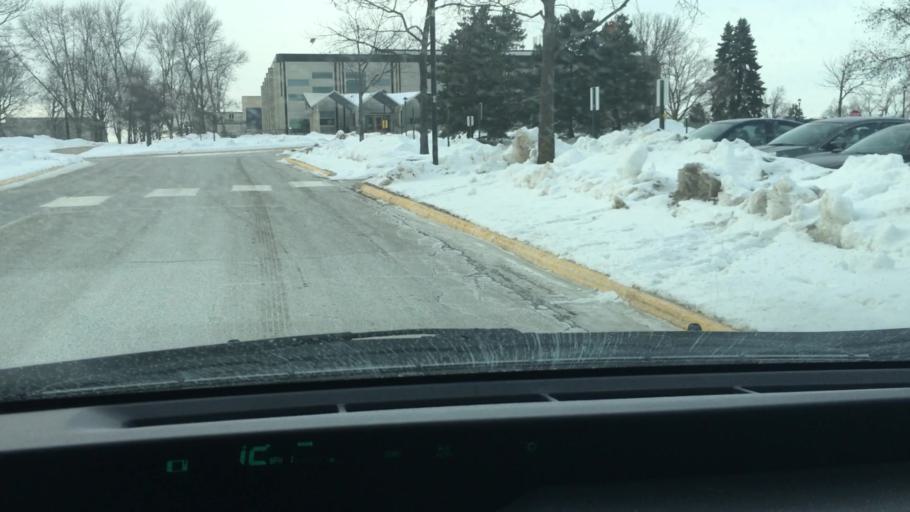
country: US
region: Minnesota
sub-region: Rice County
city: Northfield
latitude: 44.4625
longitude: -93.1832
